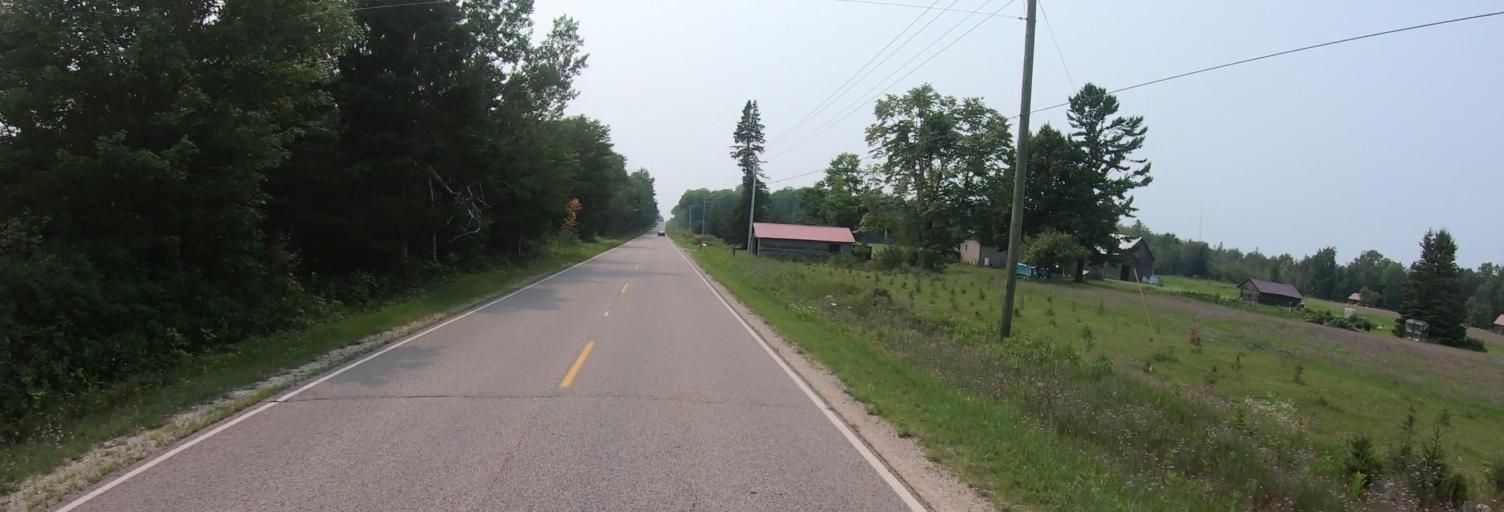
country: CA
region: Ontario
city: Thessalon
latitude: 46.0145
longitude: -84.0556
